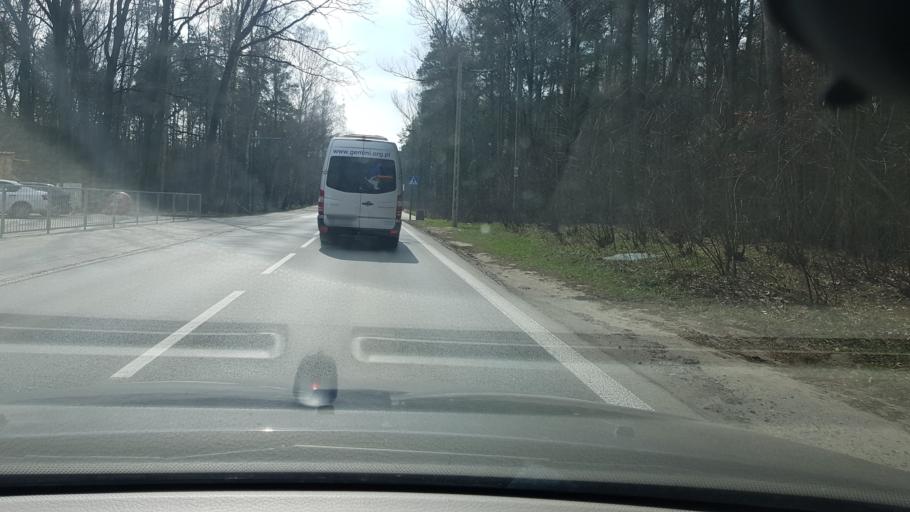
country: PL
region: Masovian Voivodeship
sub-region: Warszawa
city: Wesola
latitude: 52.2326
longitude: 21.2244
